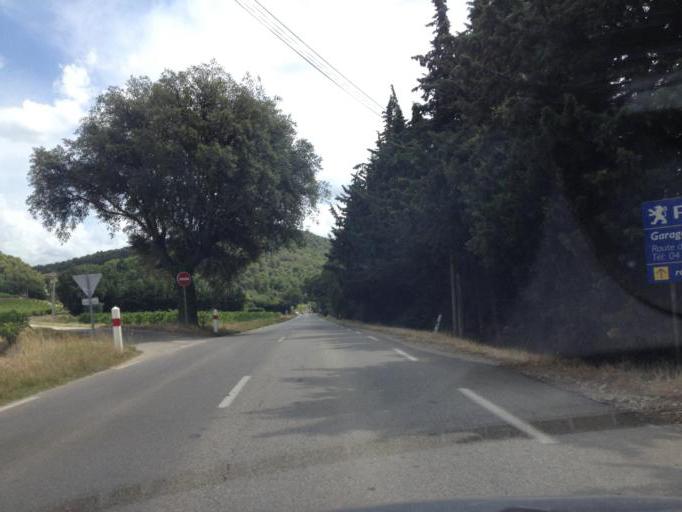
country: FR
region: Provence-Alpes-Cote d'Azur
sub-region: Departement du Vaucluse
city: Vaison-la-Romaine
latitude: 44.2475
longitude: 5.0462
